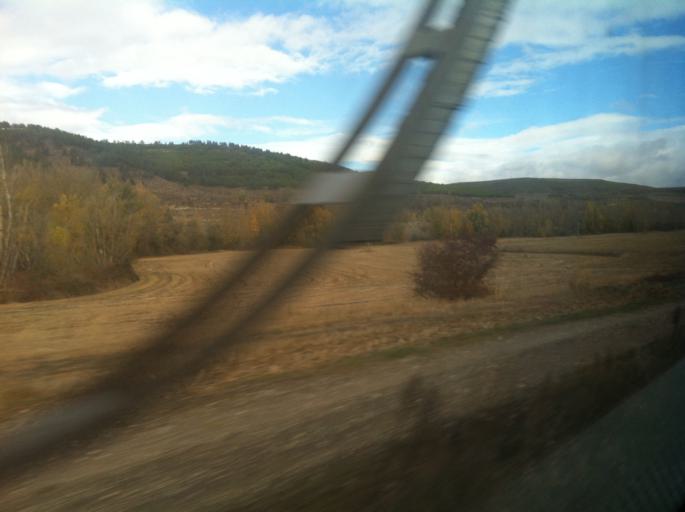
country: ES
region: Castille and Leon
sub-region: Provincia de Burgos
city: Pradanos de Bureba
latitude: 42.5153
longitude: -3.3391
